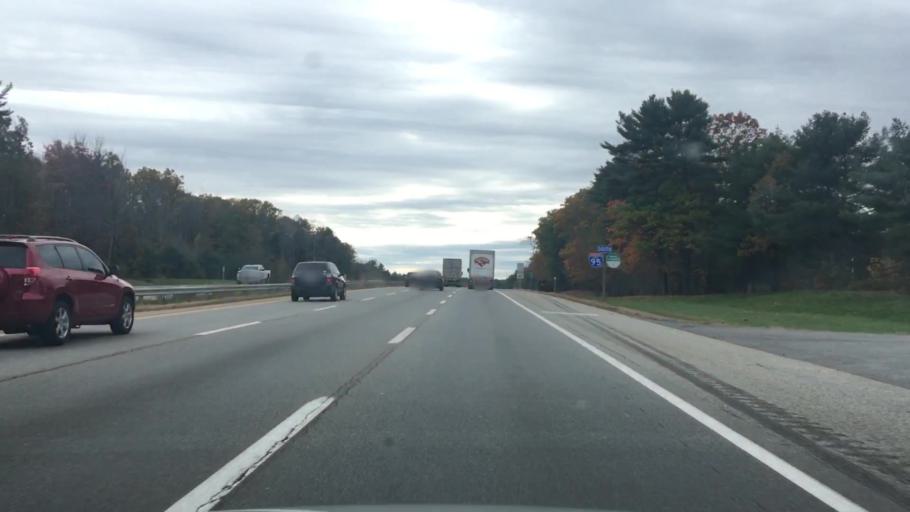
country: US
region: Maine
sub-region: Cumberland County
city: West Scarborough
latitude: 43.5994
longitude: -70.3782
